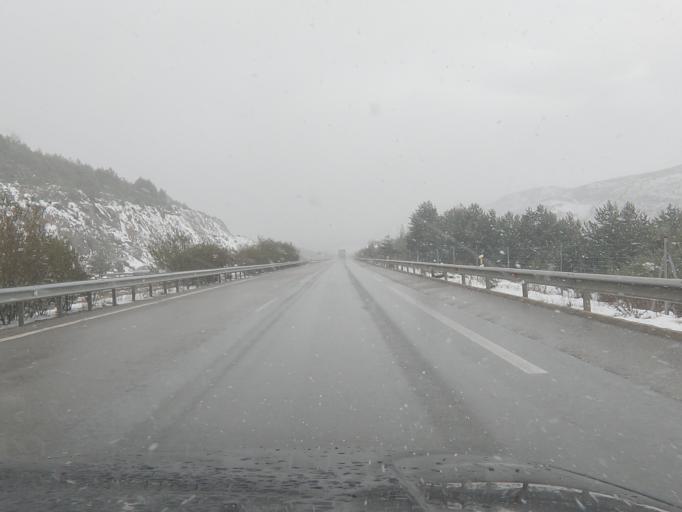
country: ES
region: Castille and Leon
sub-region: Provincia de Zamora
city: Requejo
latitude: 42.0399
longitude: -6.7765
